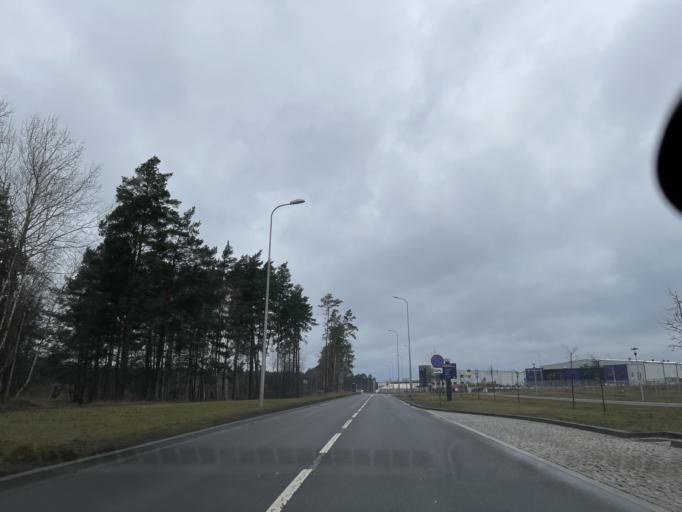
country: PL
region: Kujawsko-Pomorskie
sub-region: Bydgoszcz
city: Bydgoszcz
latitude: 53.0872
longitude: 18.0617
